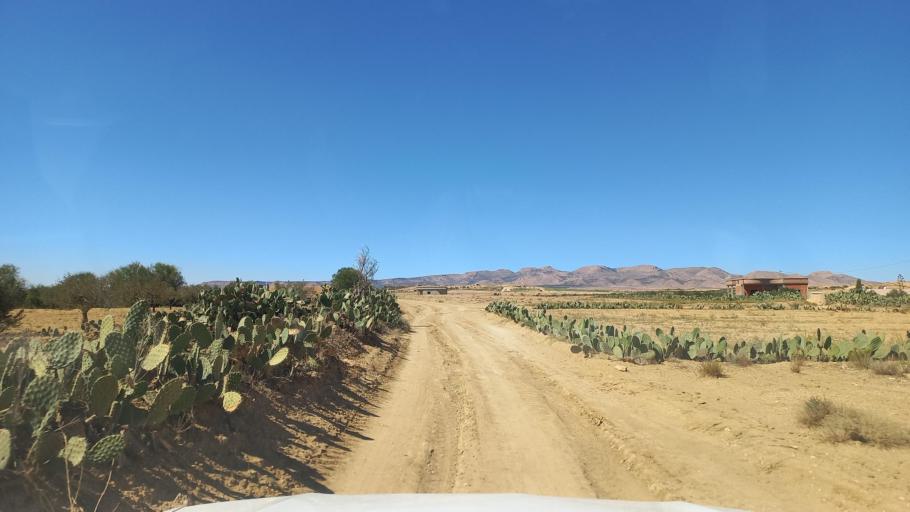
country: TN
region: Al Qasrayn
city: Sbiba
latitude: 35.3672
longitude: 9.0873
